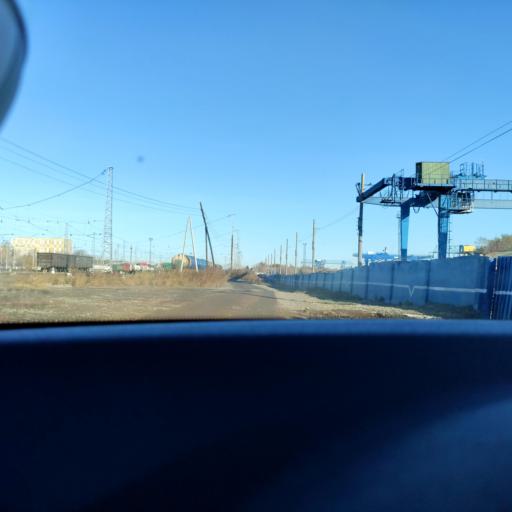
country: RU
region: Samara
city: Samara
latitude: 53.2037
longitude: 50.2488
